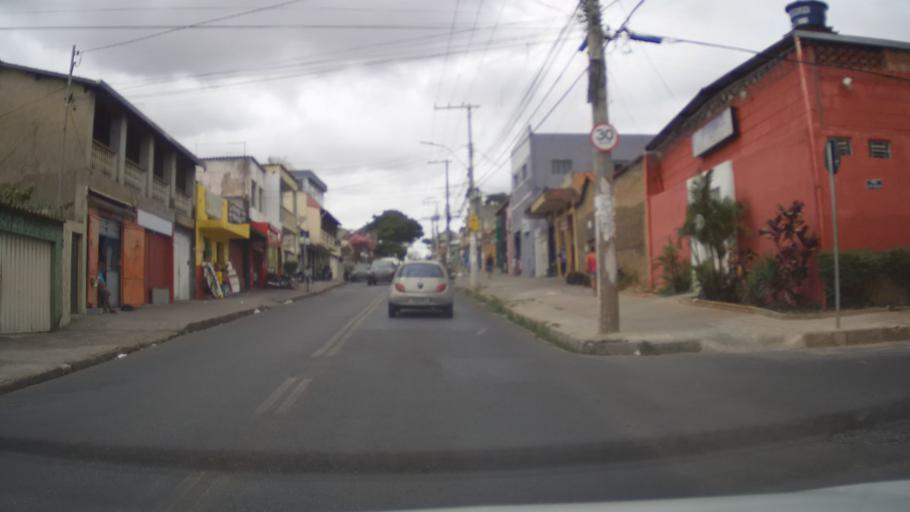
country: BR
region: Minas Gerais
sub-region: Belo Horizonte
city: Belo Horizonte
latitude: -19.8367
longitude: -43.9304
